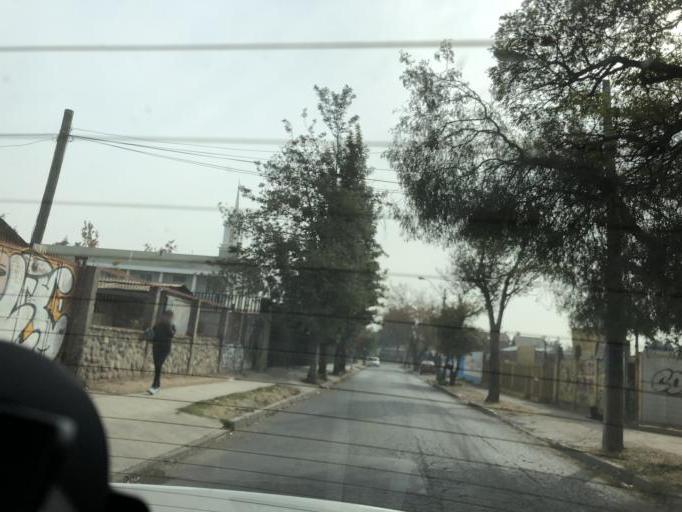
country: CL
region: Santiago Metropolitan
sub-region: Provincia de Cordillera
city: Puente Alto
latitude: -33.5614
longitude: -70.5644
